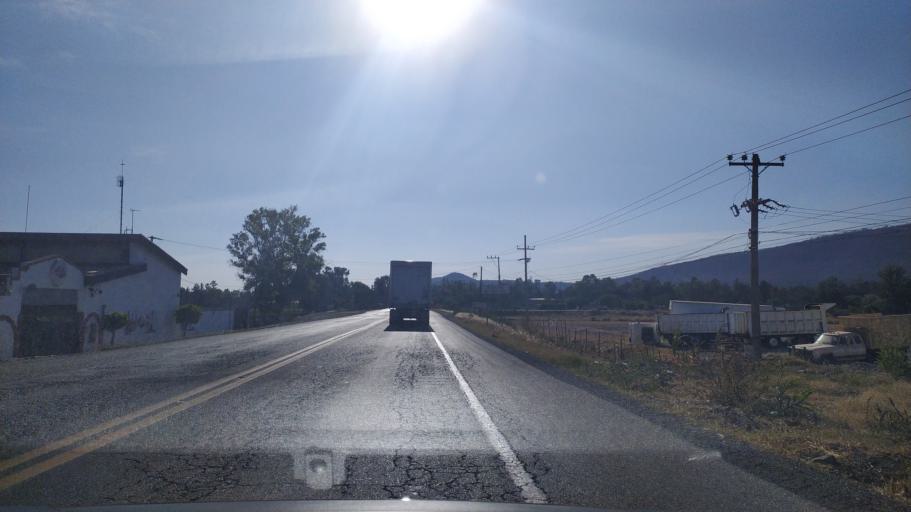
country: MX
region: Jalisco
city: Jamay
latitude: 20.2941
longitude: -102.6696
